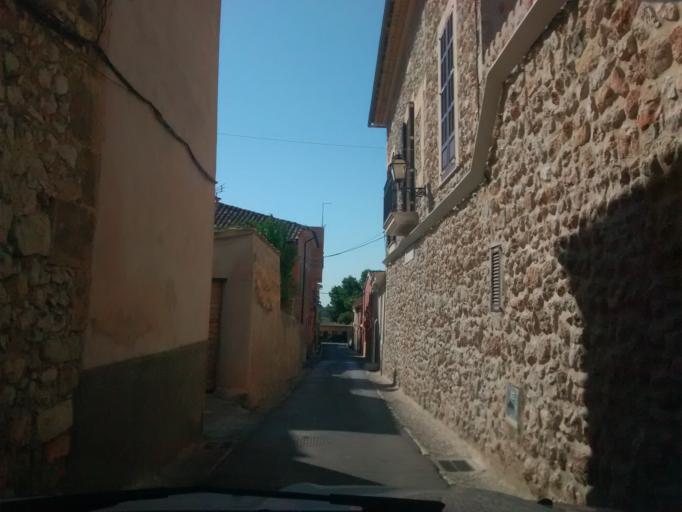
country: ES
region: Balearic Islands
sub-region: Illes Balears
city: Alaro
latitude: 39.7044
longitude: 2.7890
